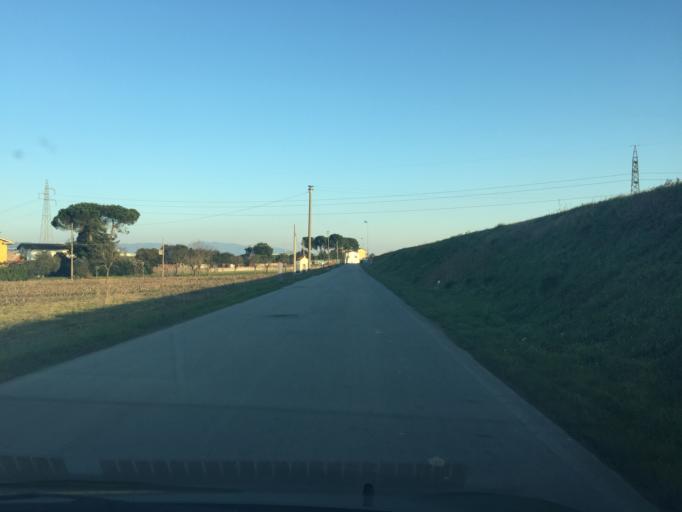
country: IT
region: Tuscany
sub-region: Provincia di Pistoia
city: Ponte Buggianese
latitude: 43.8377
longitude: 10.7537
